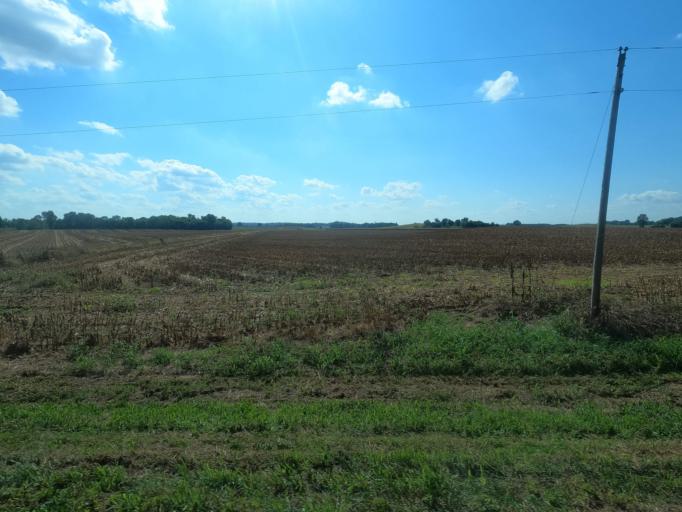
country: US
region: Illinois
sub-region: Massac County
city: Metropolis
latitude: 37.2617
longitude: -88.7594
